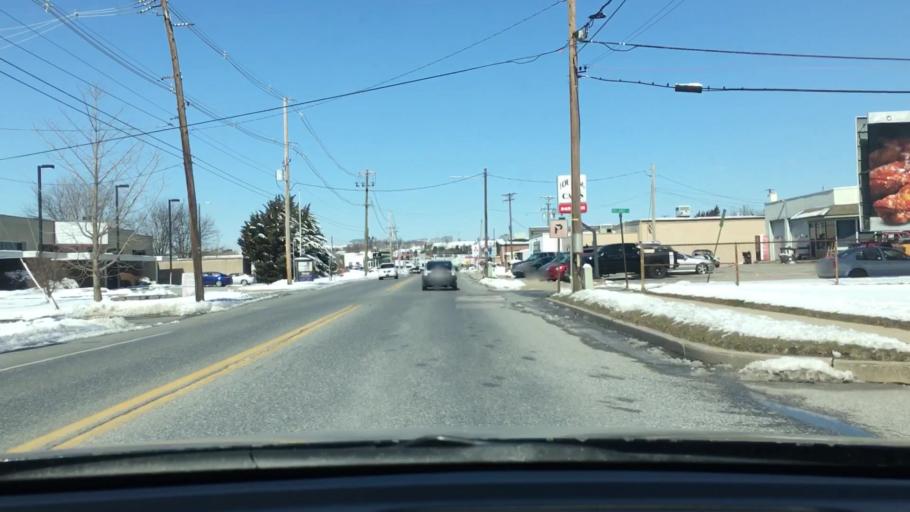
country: US
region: Pennsylvania
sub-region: York County
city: North York
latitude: 39.9753
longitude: -76.7551
